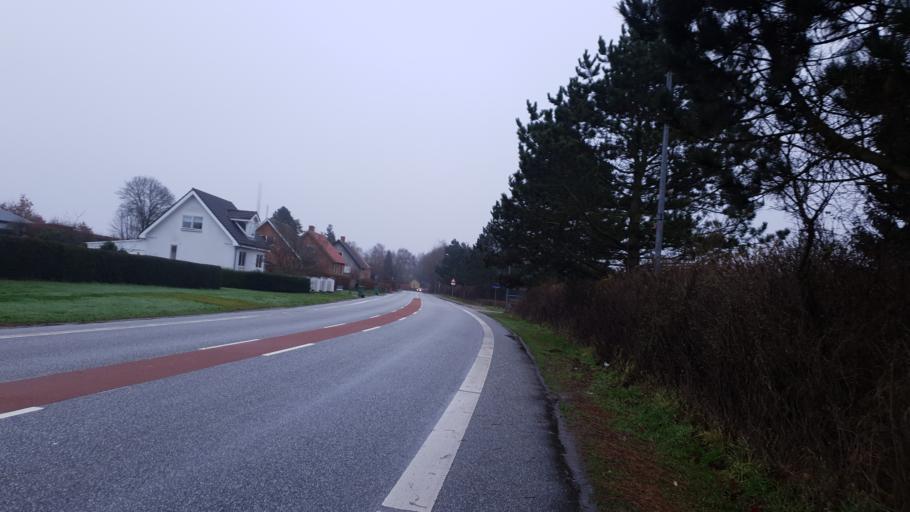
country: DK
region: Central Jutland
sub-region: Hedensted Kommune
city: Hedensted
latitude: 55.7765
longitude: 9.6963
